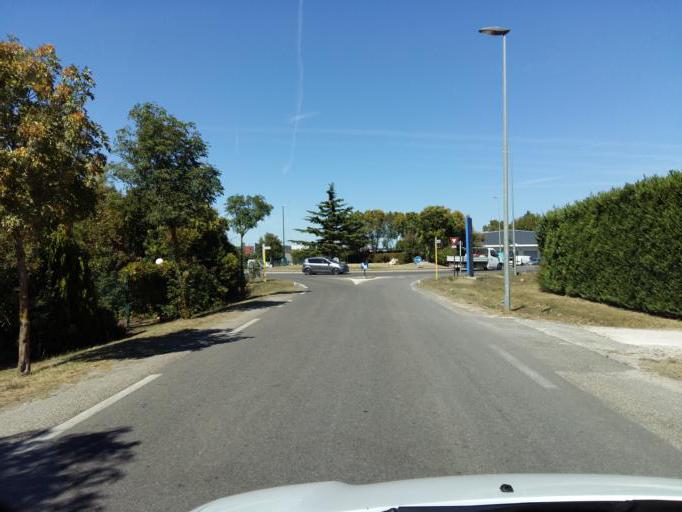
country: FR
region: Provence-Alpes-Cote d'Azur
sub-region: Departement du Vaucluse
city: Le Thor
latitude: 43.9215
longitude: 5.0189
